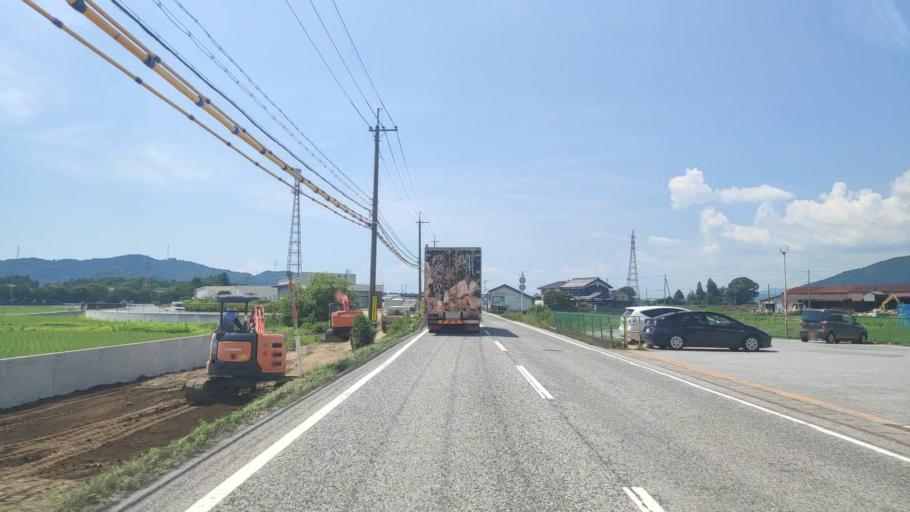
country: JP
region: Shiga Prefecture
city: Nagahama
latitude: 35.3873
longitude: 136.3629
